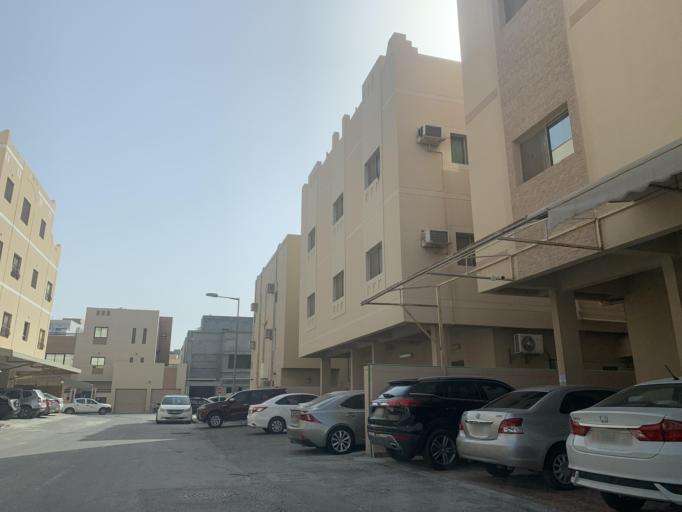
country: BH
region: Northern
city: Madinat `Isa
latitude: 26.1869
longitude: 50.5632
